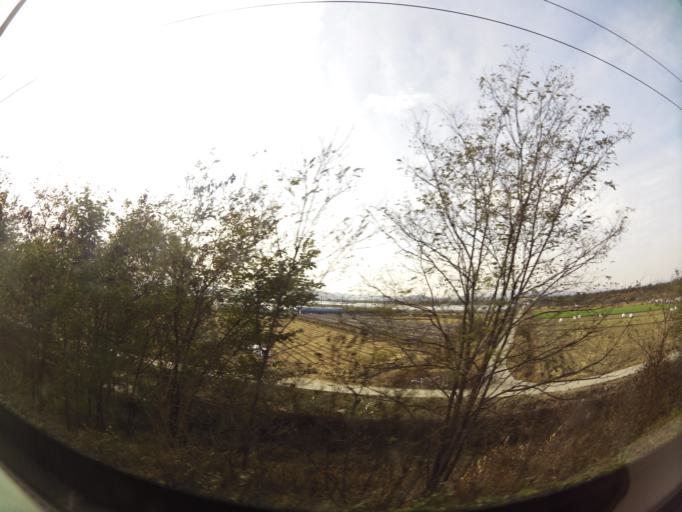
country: KR
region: Daejeon
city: Songgang-dong
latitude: 36.5678
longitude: 127.3174
